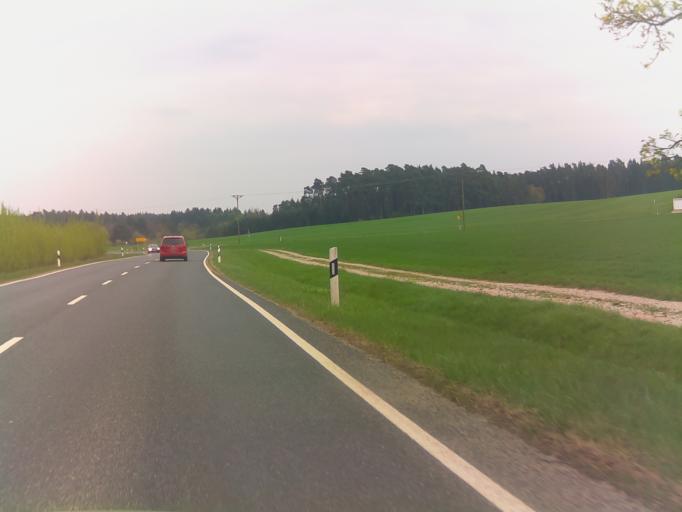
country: DE
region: Bavaria
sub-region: Regierungsbezirk Mittelfranken
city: Schnaittach
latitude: 49.5714
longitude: 11.3013
